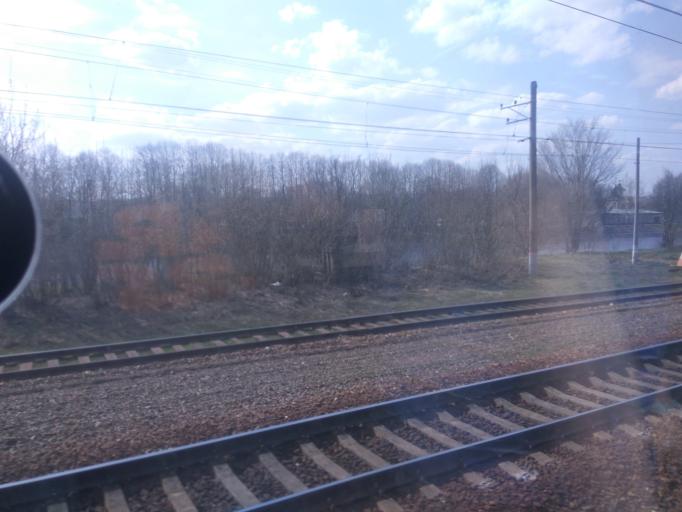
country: RU
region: Moskovskaya
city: Yakhroma
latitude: 56.2840
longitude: 37.5037
